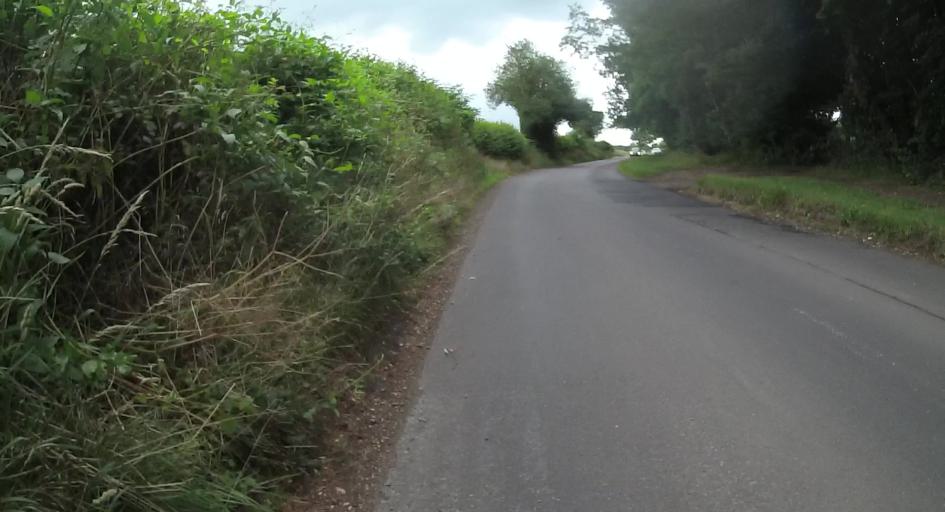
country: GB
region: England
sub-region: Surrey
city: Farnham
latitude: 51.2277
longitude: -0.8551
